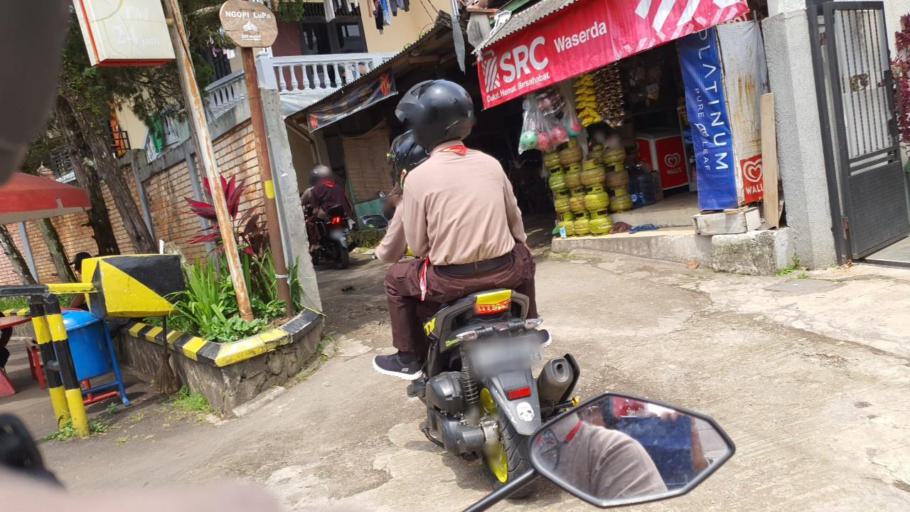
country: ID
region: West Java
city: Caringin
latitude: -6.6516
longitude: 106.8985
